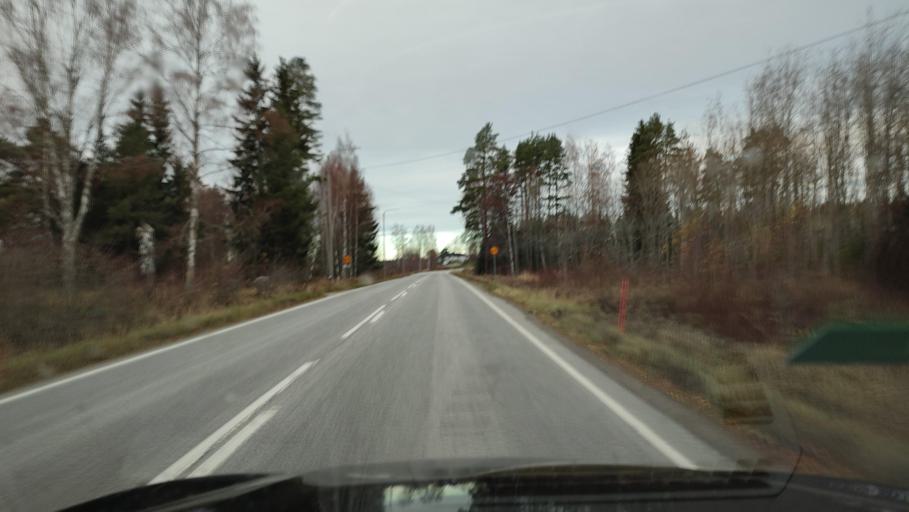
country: FI
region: Ostrobothnia
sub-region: Sydosterbotten
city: Naerpes
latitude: 62.4173
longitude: 21.3438
